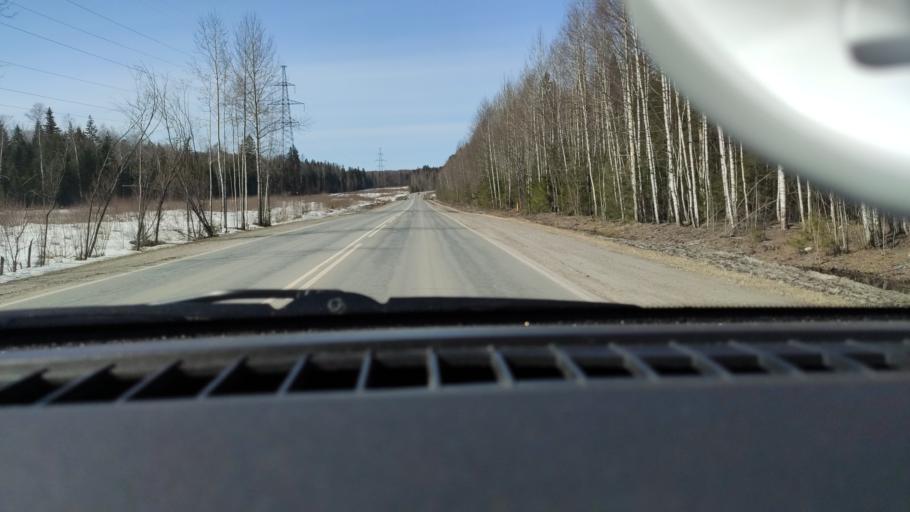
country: RU
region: Perm
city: Perm
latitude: 58.1370
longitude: 56.2862
